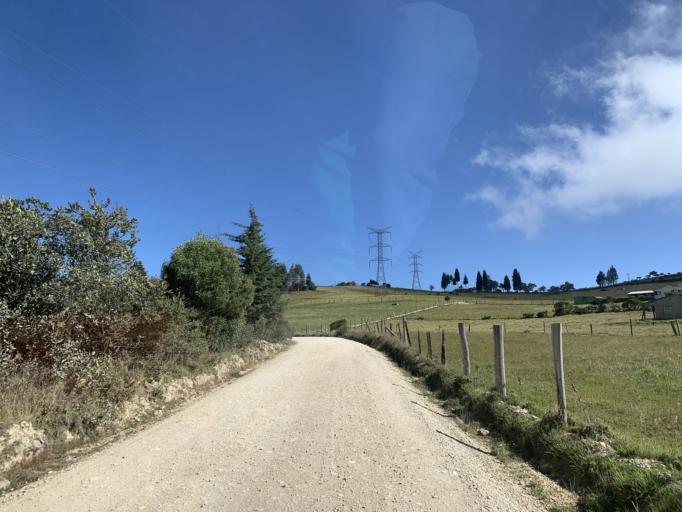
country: CO
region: Boyaca
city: Tuta
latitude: 5.7004
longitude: -73.1487
